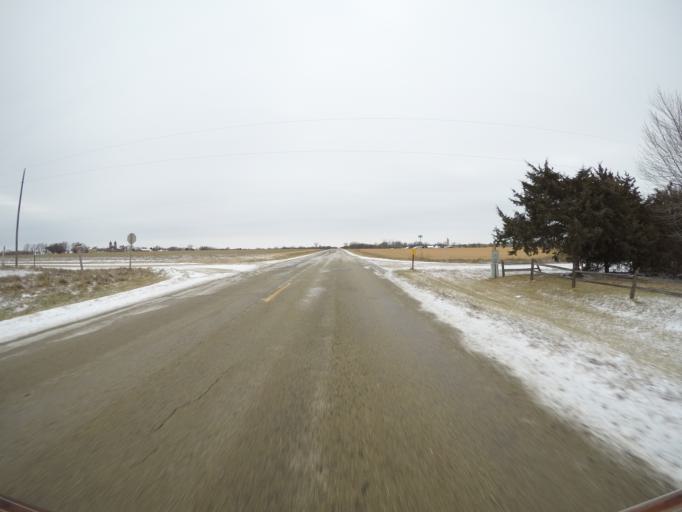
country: US
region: Kansas
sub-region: Wabaunsee County
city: Alma
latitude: 39.0799
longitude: -96.1690
